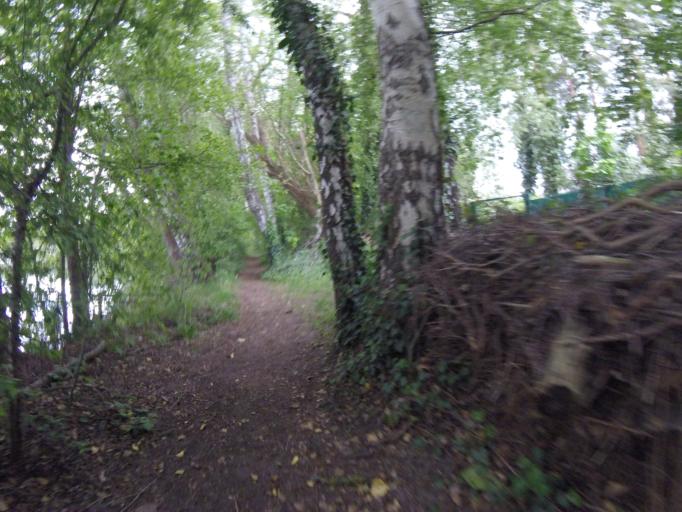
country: DE
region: Brandenburg
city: Bestensee
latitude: 52.2578
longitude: 13.6655
